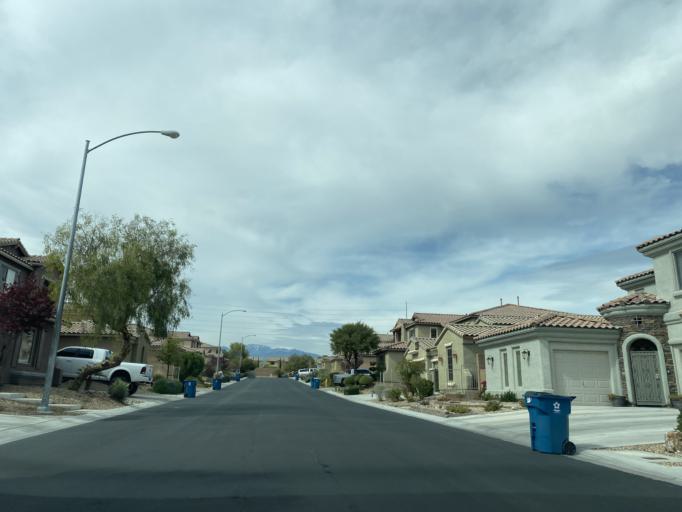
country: US
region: Nevada
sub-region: Clark County
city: Summerlin South
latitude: 36.3043
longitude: -115.3122
